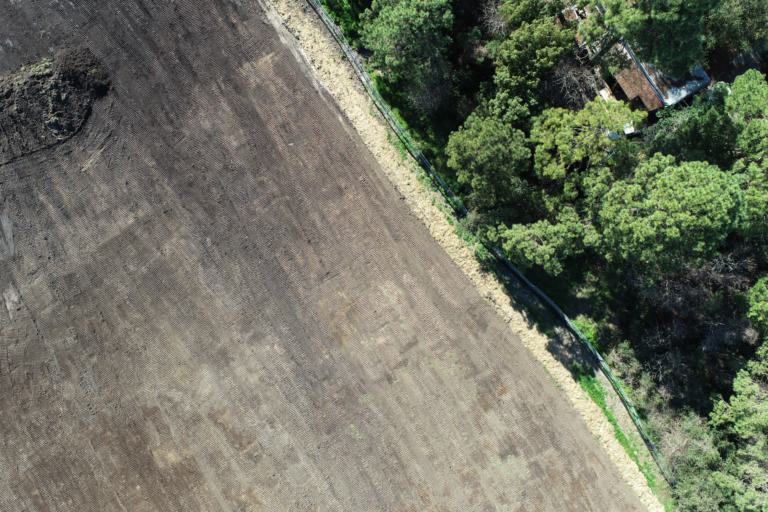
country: US
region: Georgia
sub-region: Chatham County
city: Wilmington Island
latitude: 32.0201
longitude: -80.9716
